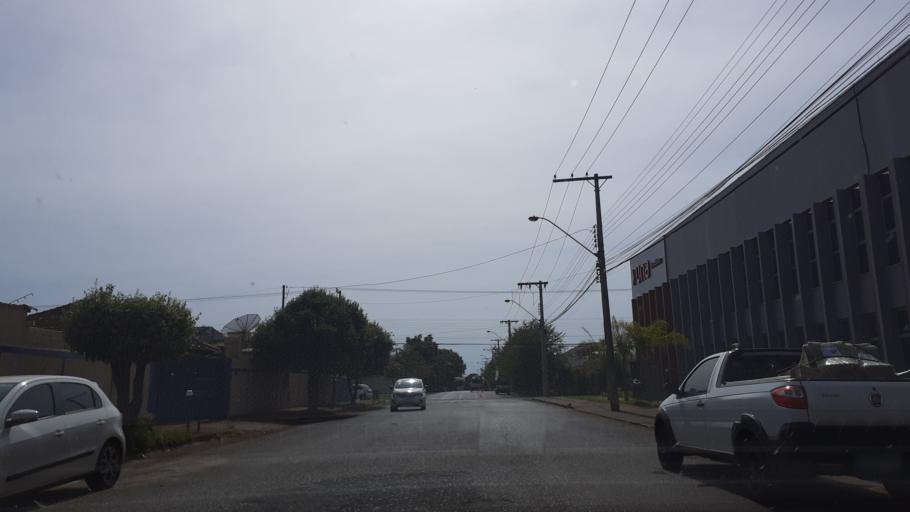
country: BR
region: Goias
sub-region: Itumbiara
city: Itumbiara
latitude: -18.4172
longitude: -49.2319
